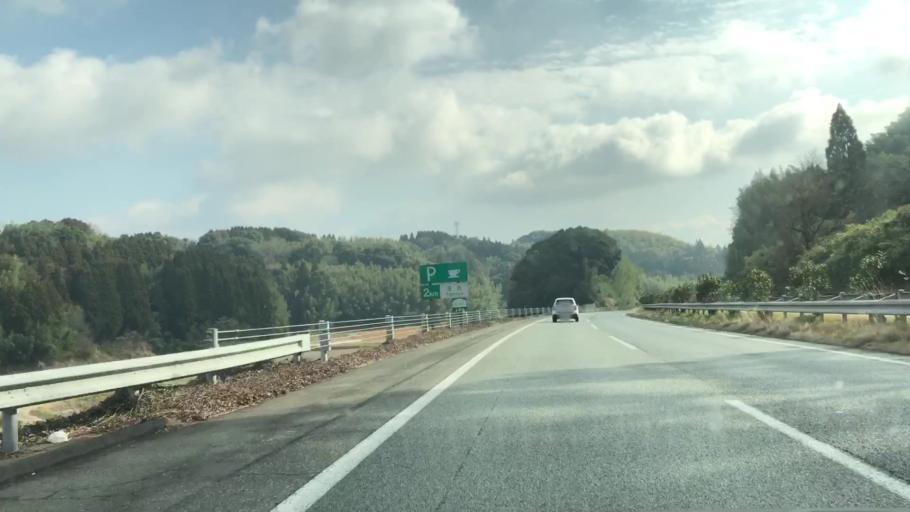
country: JP
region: Kumamoto
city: Yamaga
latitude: 33.0294
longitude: 130.5755
